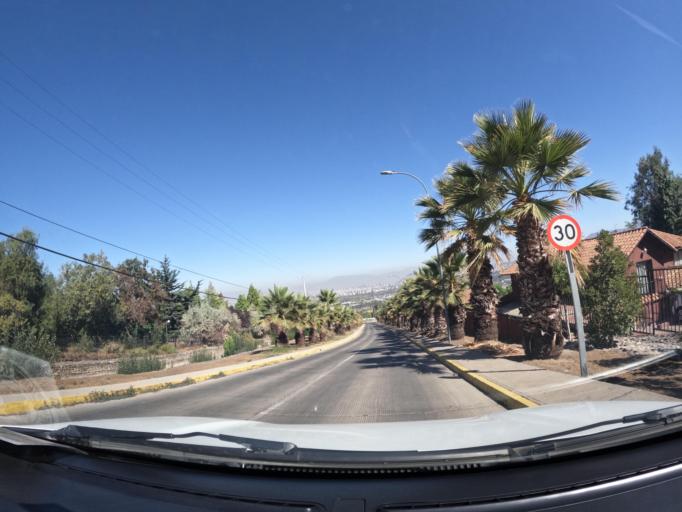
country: CL
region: Santiago Metropolitan
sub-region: Provincia de Santiago
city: Villa Presidente Frei, Nunoa, Santiago, Chile
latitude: -33.4639
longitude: -70.5194
